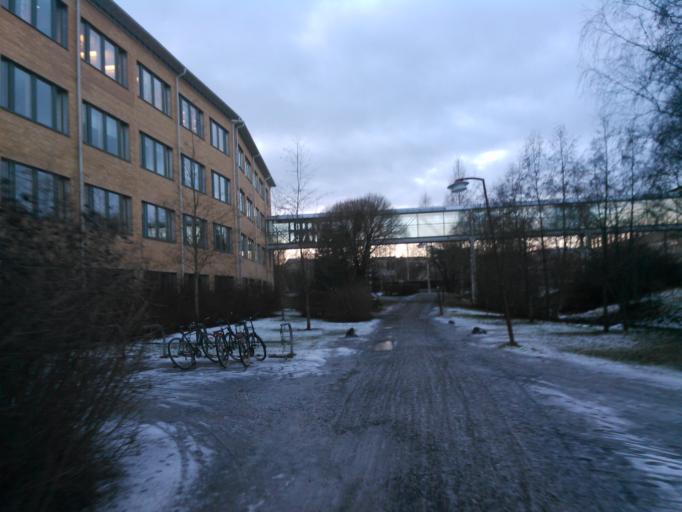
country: SE
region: Vaesterbotten
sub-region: Umea Kommun
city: Umea
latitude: 63.8208
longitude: 20.3084
